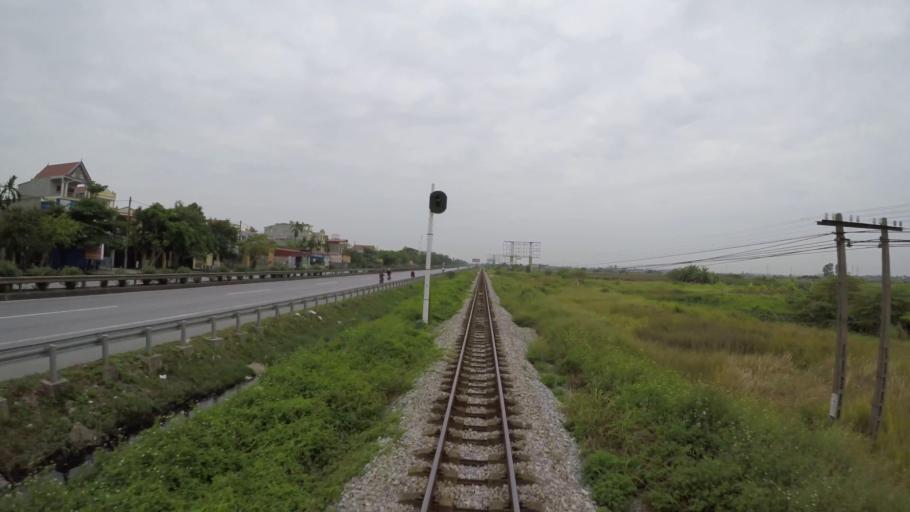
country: VN
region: Hai Duong
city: Phu Thai
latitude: 20.9398
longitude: 106.5466
